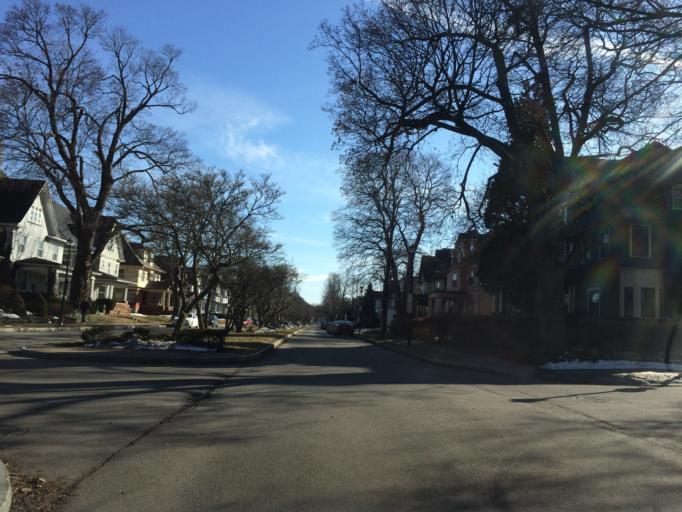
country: US
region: New York
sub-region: Monroe County
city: Rochester
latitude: 43.1472
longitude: -77.5878
